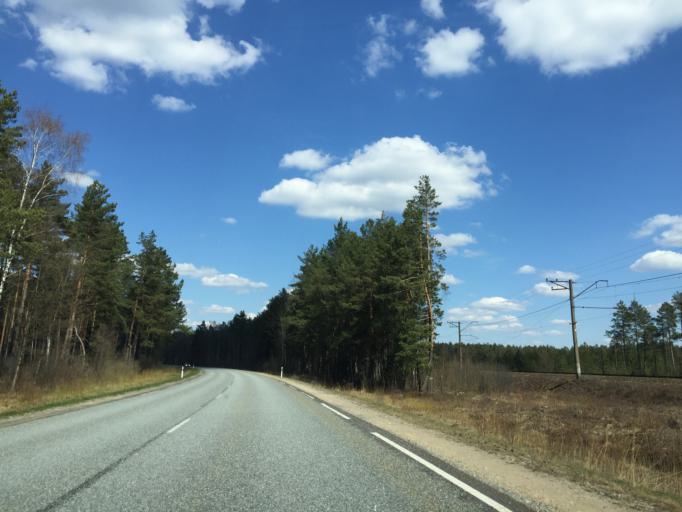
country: LV
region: Saulkrastu
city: Saulkrasti
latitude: 57.2074
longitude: 24.3794
